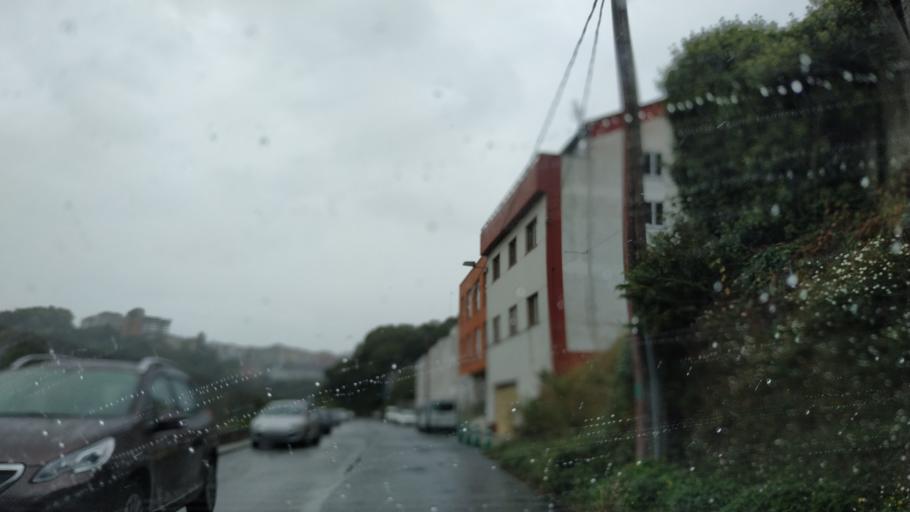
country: ES
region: Galicia
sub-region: Provincia de Lugo
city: Lugo
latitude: 43.0005
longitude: -7.5684
